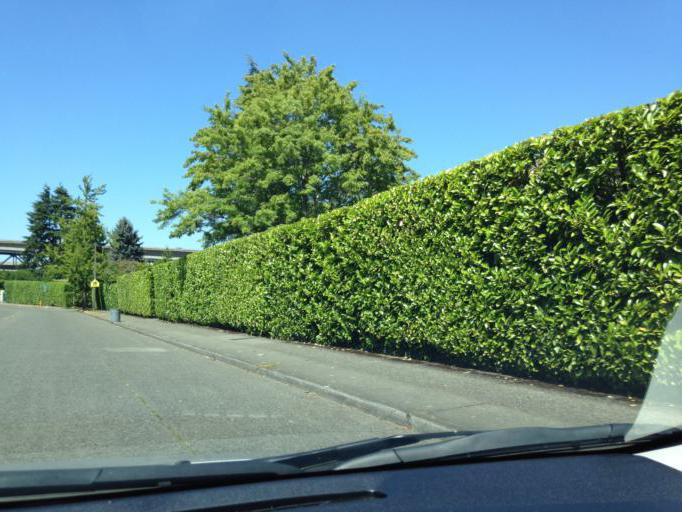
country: US
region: Washington
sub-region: King County
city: Seattle
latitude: 47.5879
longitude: -122.2862
